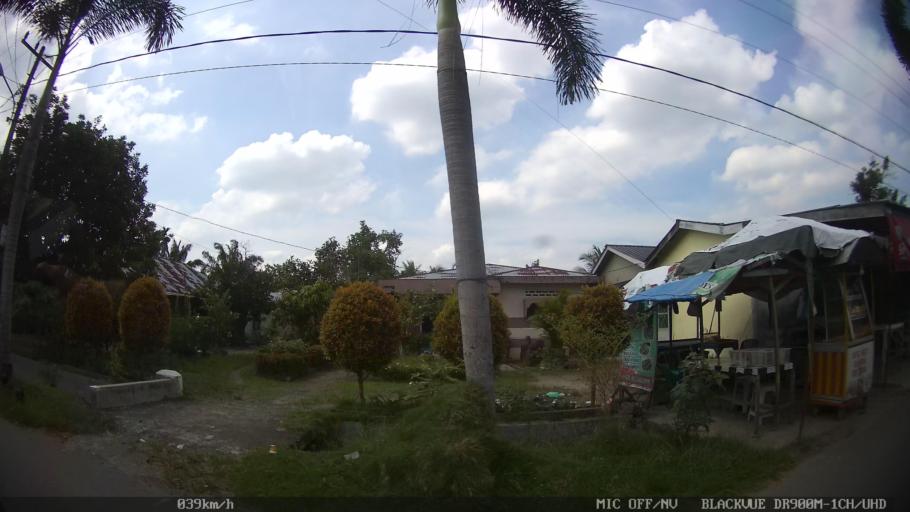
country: ID
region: North Sumatra
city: Binjai
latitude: 3.6354
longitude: 98.5046
